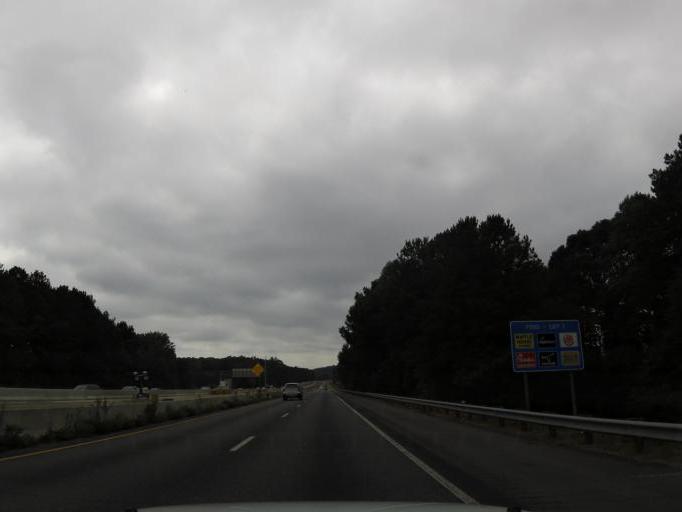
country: US
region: Georgia
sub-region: Cobb County
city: Kennesaw
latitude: 34.0272
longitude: -84.5605
